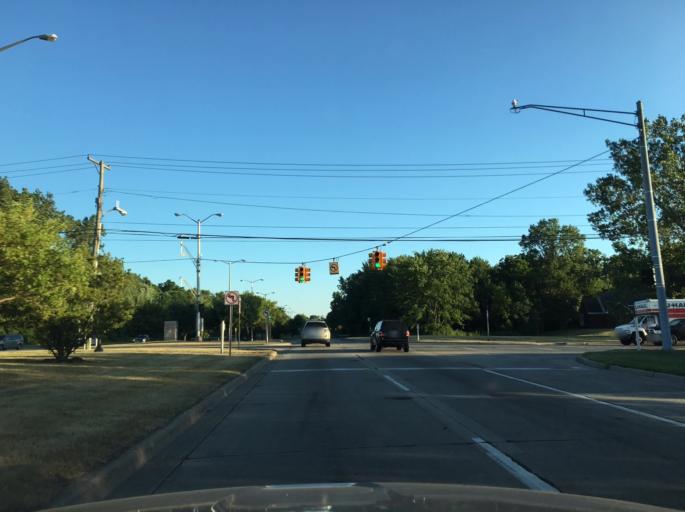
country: US
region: Michigan
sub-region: Macomb County
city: Sterling Heights
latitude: 42.5890
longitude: -82.9916
